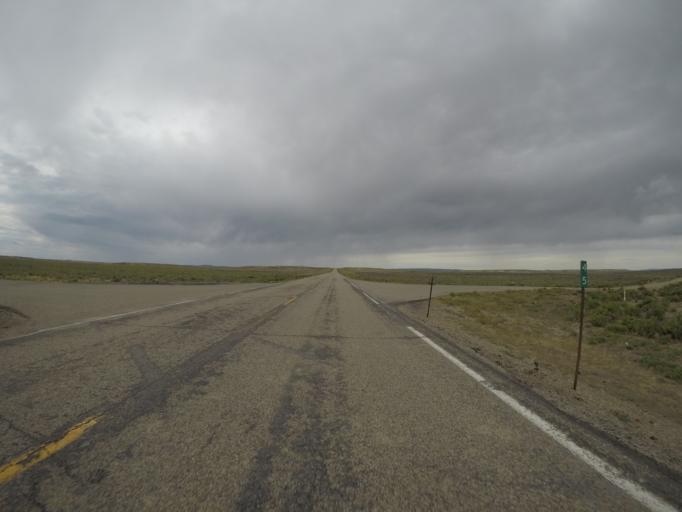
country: US
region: Wyoming
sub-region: Lincoln County
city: Kemmerer
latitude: 41.9636
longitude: -110.1428
